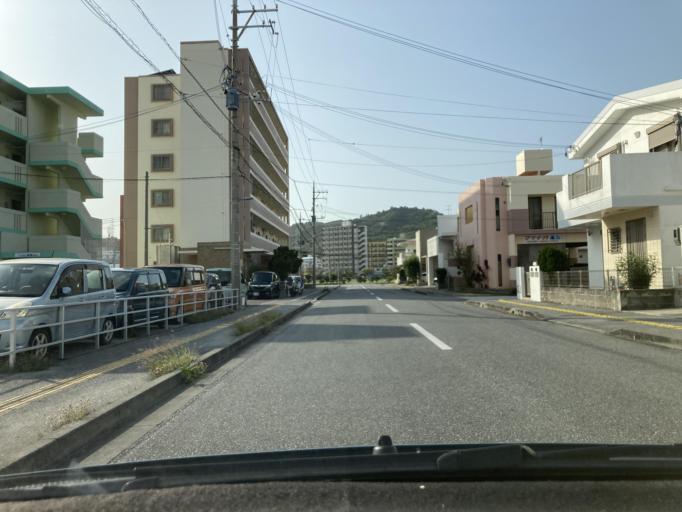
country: JP
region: Okinawa
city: Ginowan
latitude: 26.2067
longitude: 127.7608
